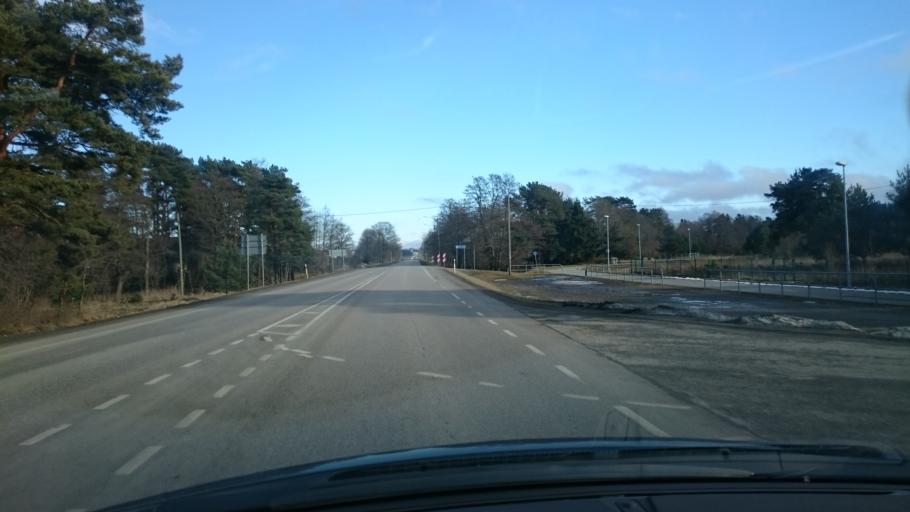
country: EE
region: Harju
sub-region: Harku vald
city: Tabasalu
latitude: 59.4314
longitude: 24.6018
